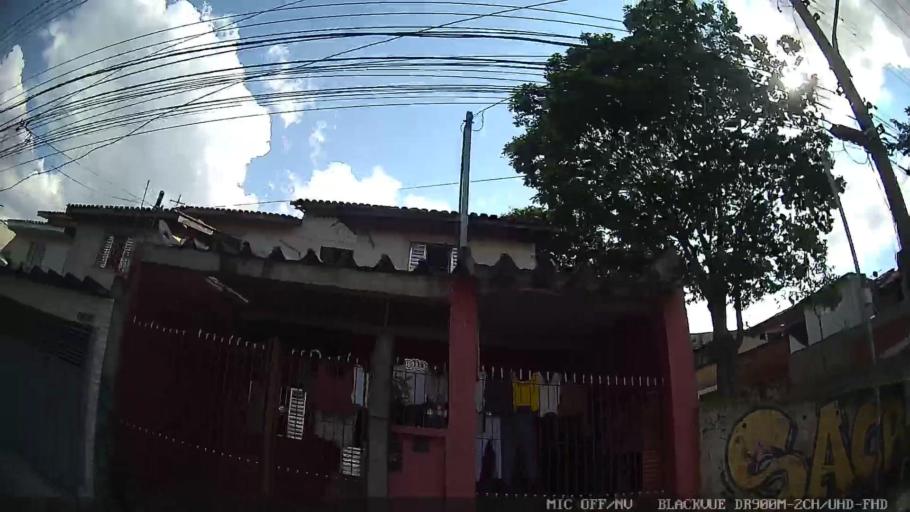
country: BR
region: Sao Paulo
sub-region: Ferraz De Vasconcelos
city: Ferraz de Vasconcelos
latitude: -23.5370
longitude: -46.4159
